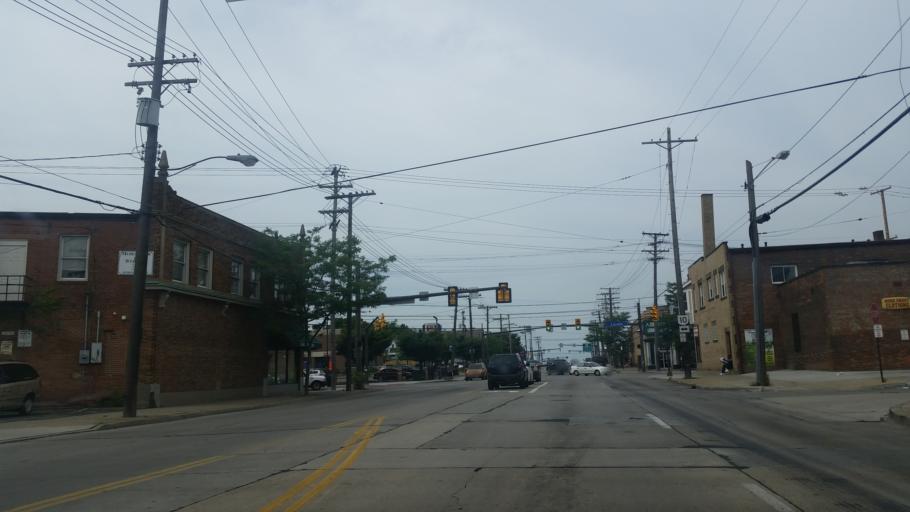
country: US
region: Ohio
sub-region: Cuyahoga County
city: Lakewood
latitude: 41.4613
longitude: -81.7689
